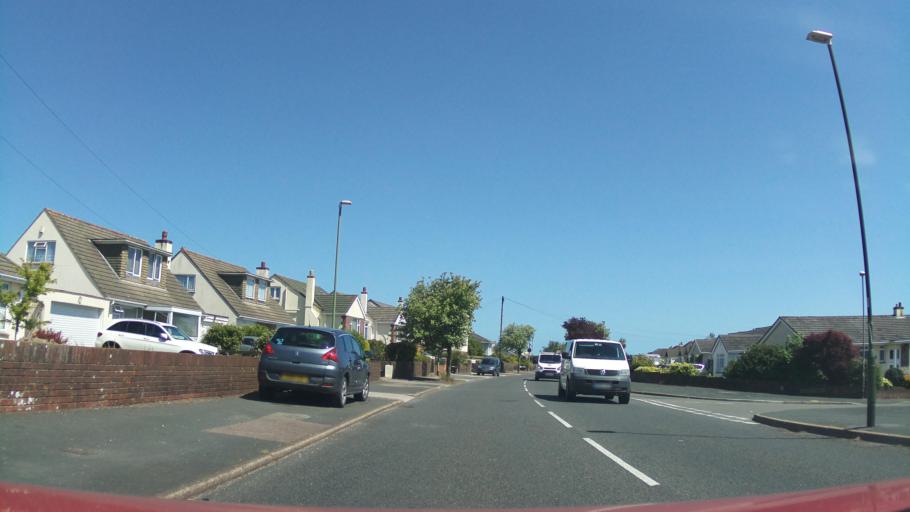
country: GB
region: England
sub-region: Devon
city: Marldon
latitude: 50.4558
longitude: -3.5769
